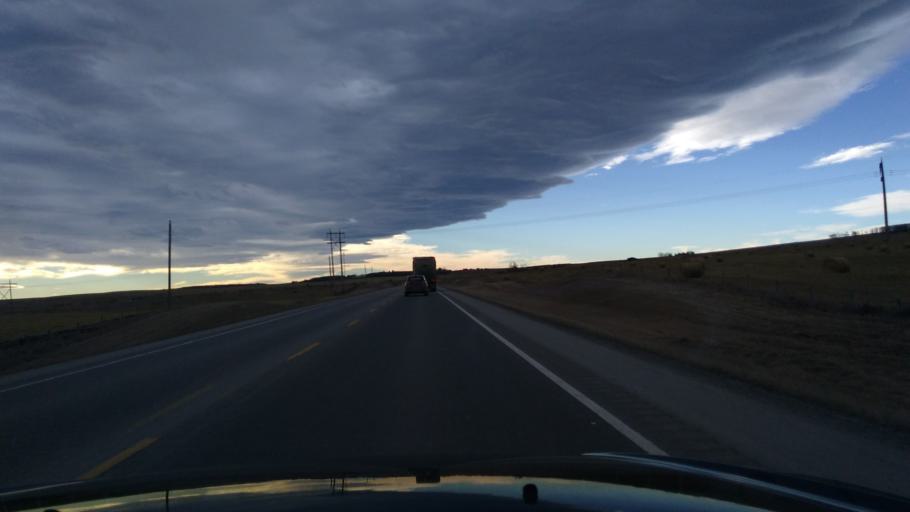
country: CA
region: Alberta
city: Cochrane
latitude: 51.1219
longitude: -114.4668
